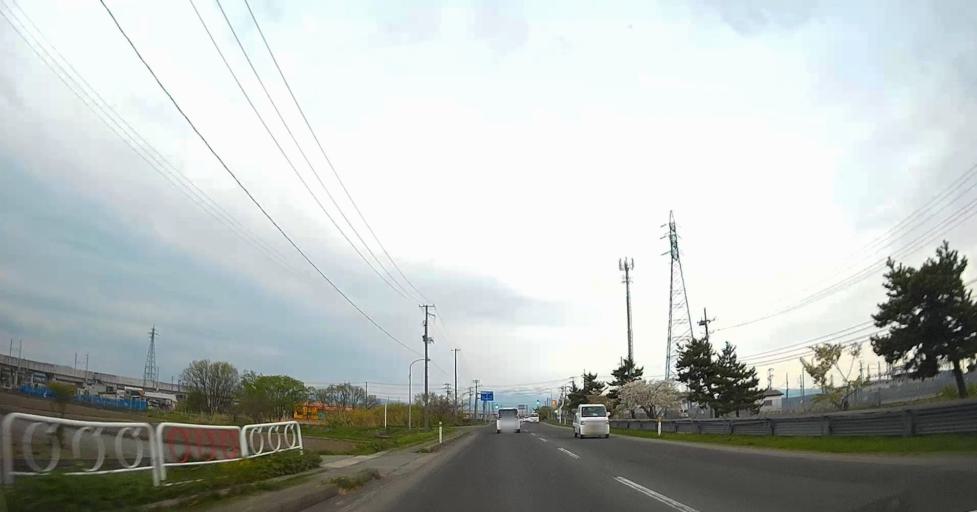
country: JP
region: Aomori
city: Aomori Shi
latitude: 40.8445
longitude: 140.6863
